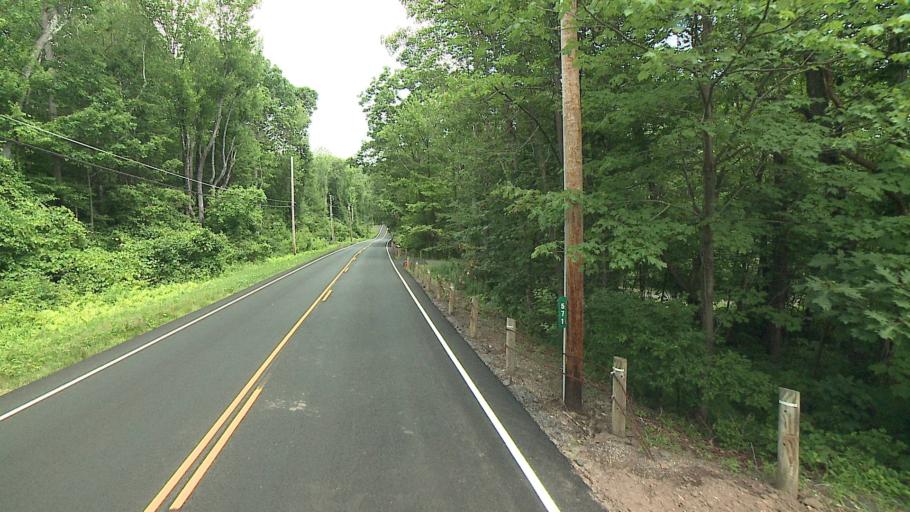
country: US
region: Massachusetts
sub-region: Hampden County
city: Granville
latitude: 42.0317
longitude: -72.8851
